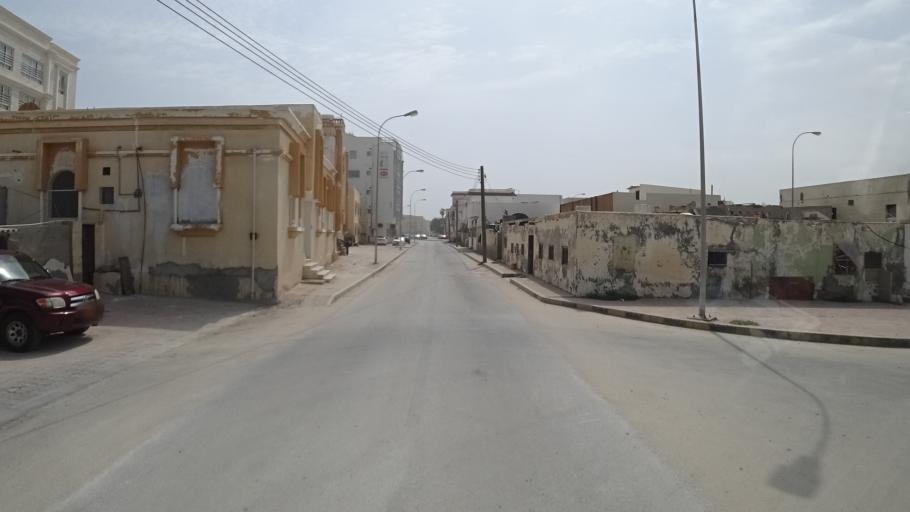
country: OM
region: Zufar
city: Salalah
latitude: 17.0100
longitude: 54.1632
